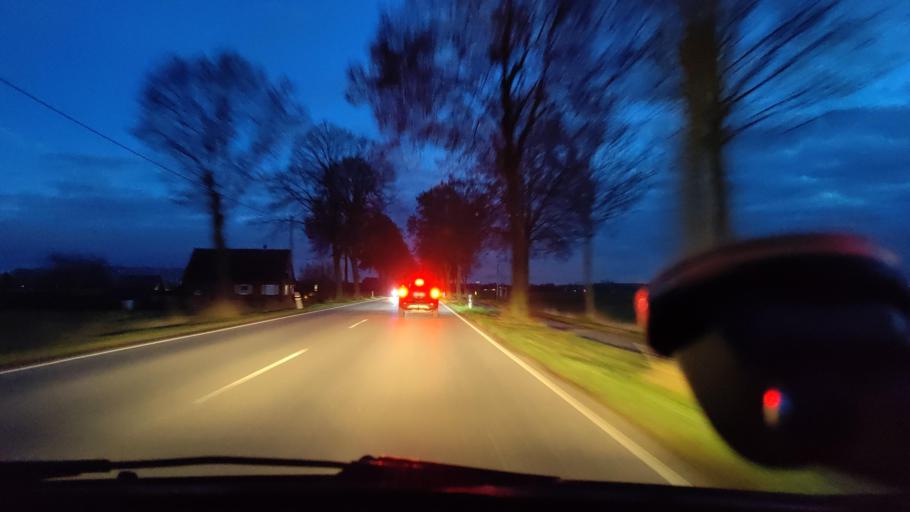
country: DE
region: North Rhine-Westphalia
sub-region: Regierungsbezirk Dusseldorf
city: Xanten
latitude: 51.6883
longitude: 6.3992
